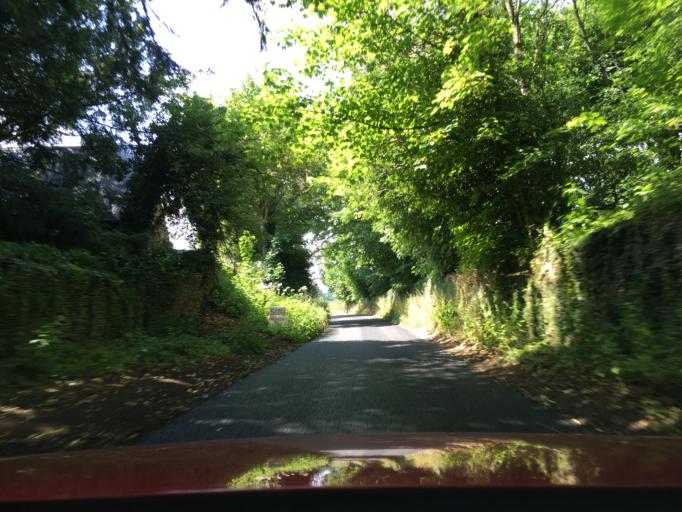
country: GB
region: England
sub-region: Gloucestershire
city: Tetbury
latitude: 51.6557
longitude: -2.1854
